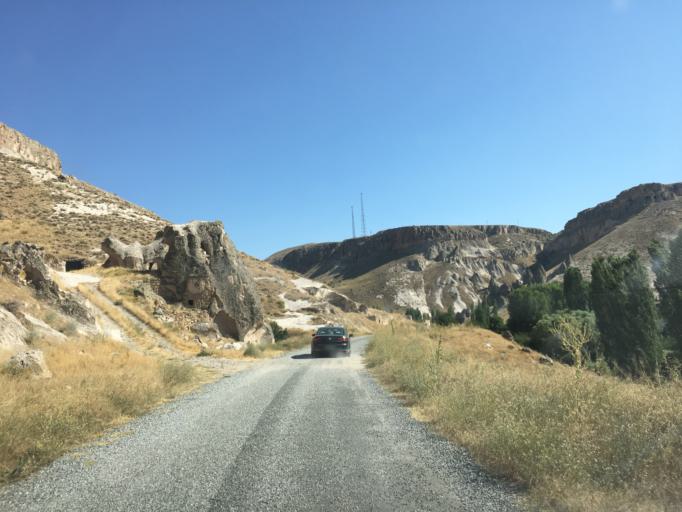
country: TR
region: Kayseri
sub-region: Yesilhisar
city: Yesilhisar
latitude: 38.3479
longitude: 34.9702
